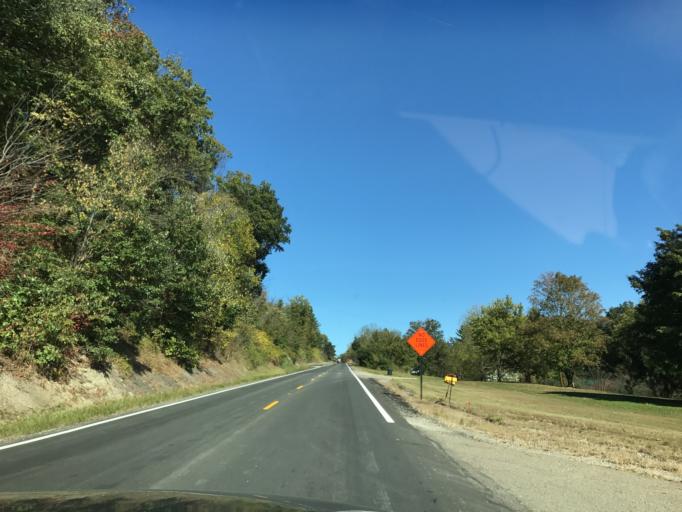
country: US
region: Ohio
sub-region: Guernsey County
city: Byesville
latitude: 40.0239
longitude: -81.5085
